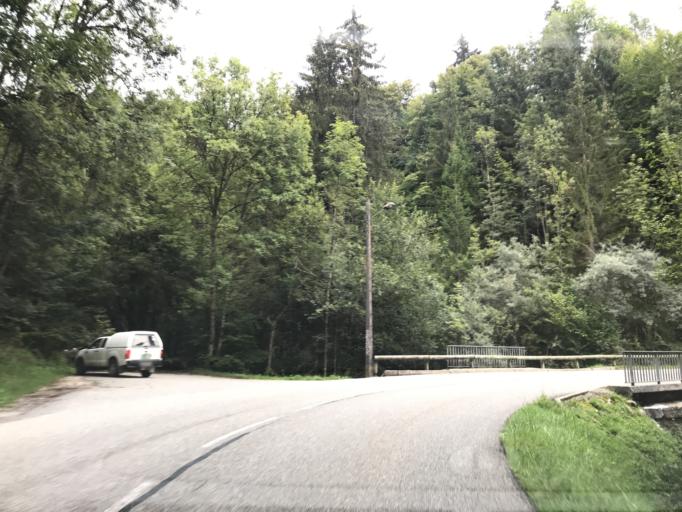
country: FR
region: Rhone-Alpes
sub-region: Departement de la Haute-Savoie
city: Talloires
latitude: 45.8329
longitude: 6.2413
